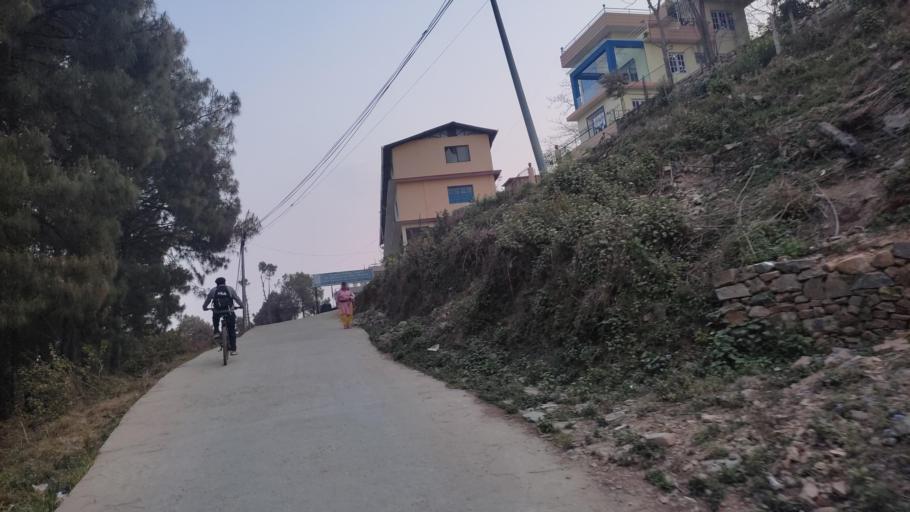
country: NP
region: Central Region
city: Kirtipur
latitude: 27.6669
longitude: 85.2936
